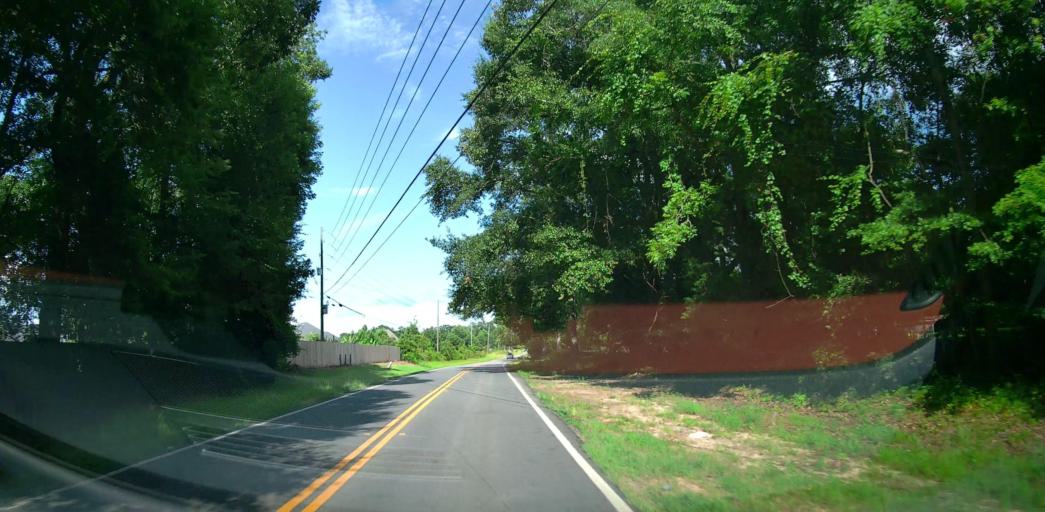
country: US
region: Georgia
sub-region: Houston County
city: Centerville
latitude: 32.5350
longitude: -83.6672
